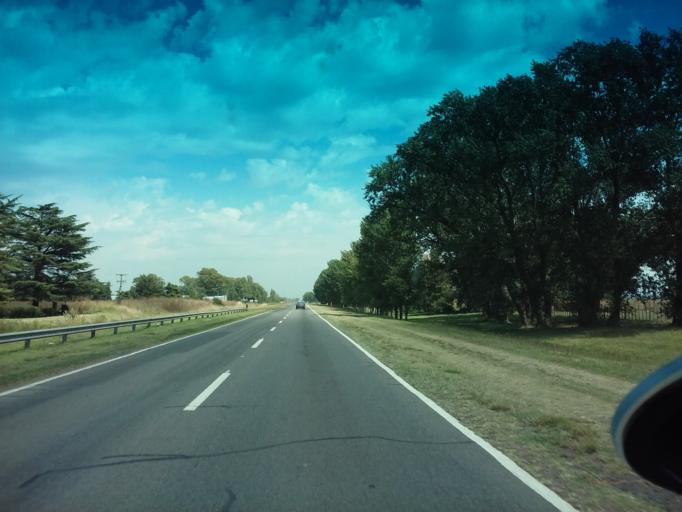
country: AR
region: Buenos Aires
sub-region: Partido de Carlos Casares
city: Carlos Casares
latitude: -35.6286
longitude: -61.3351
